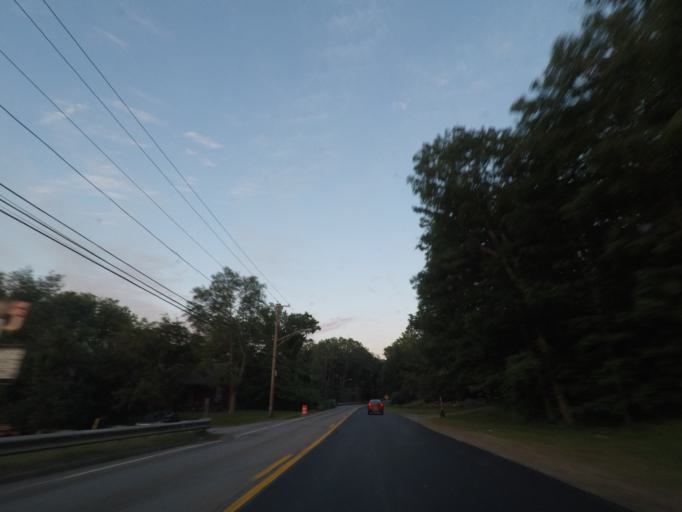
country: US
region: Massachusetts
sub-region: Worcester County
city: Southbridge
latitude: 42.0589
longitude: -71.9980
